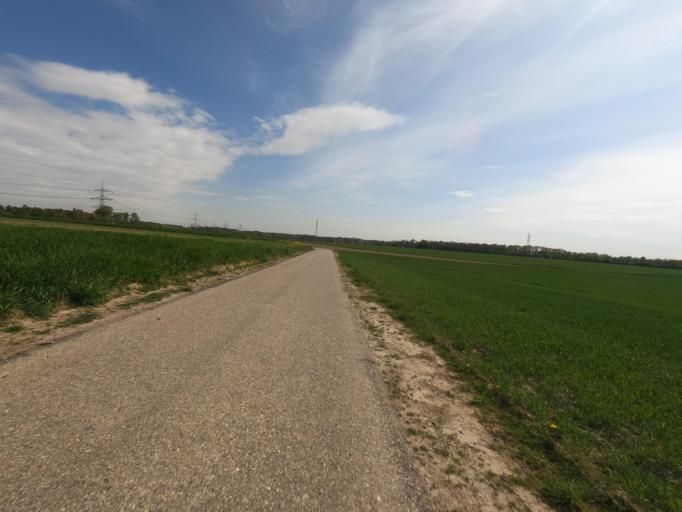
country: DE
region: North Rhine-Westphalia
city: Geilenkirchen
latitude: 50.9812
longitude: 6.1274
